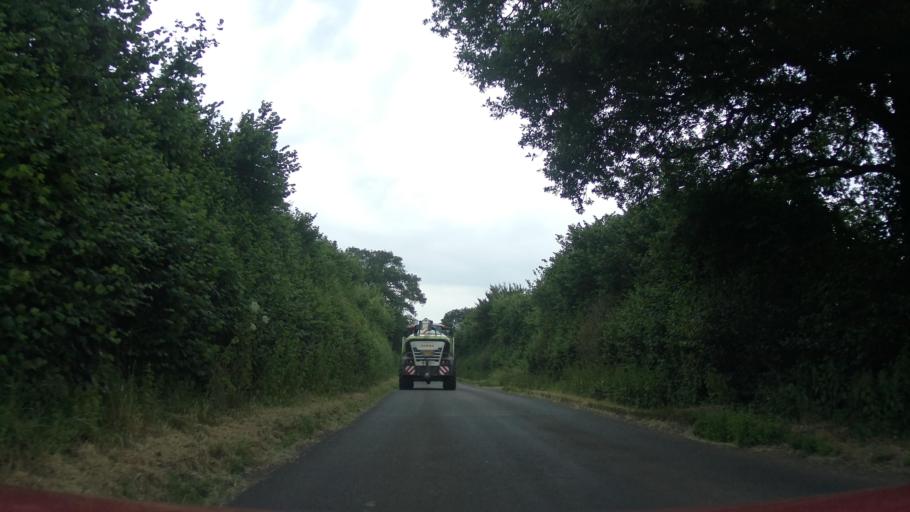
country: GB
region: England
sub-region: Somerset
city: Yeovil
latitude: 50.9174
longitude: -2.5855
